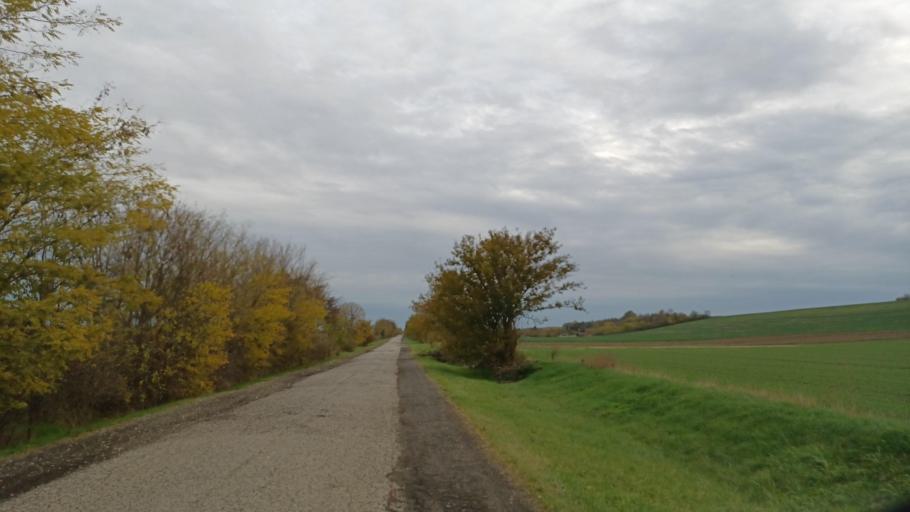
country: HU
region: Tolna
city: Simontornya
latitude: 46.6957
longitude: 18.5901
